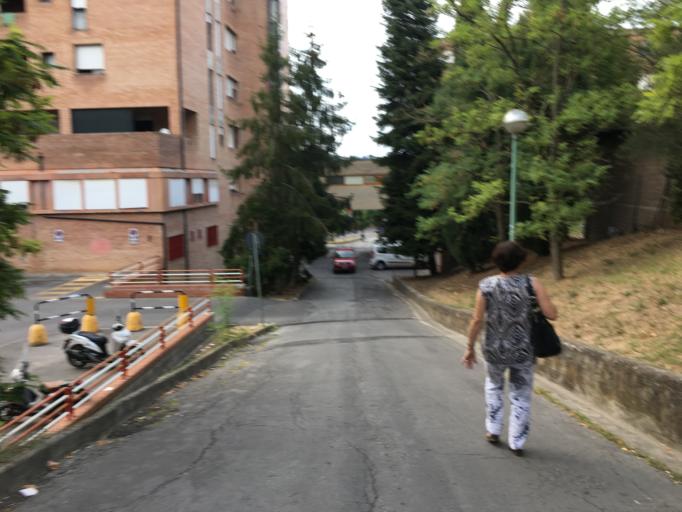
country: IT
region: Tuscany
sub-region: Provincia di Siena
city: Belverde
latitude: 43.3361
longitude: 11.3010
